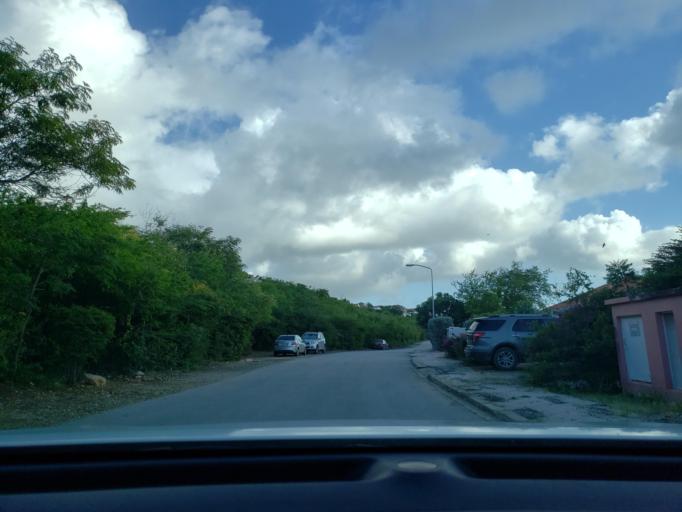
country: CW
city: Dorp Soto
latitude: 12.2033
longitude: -69.0780
